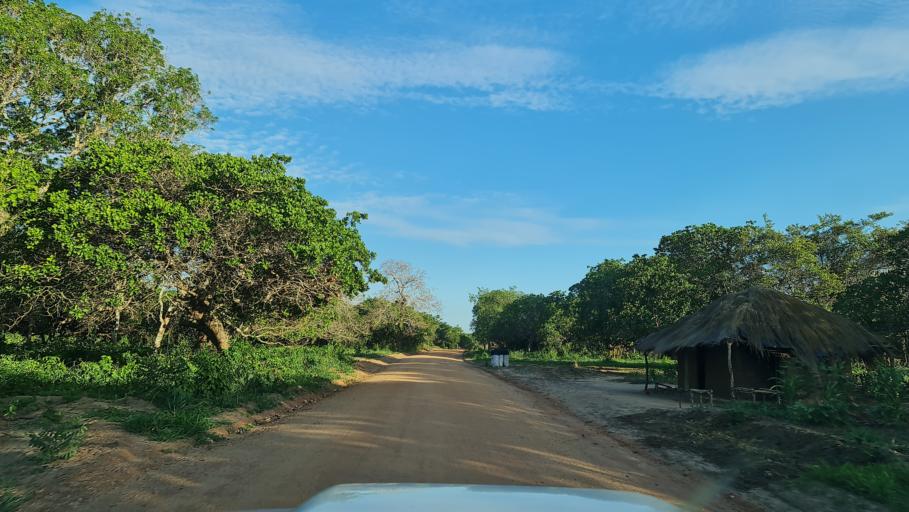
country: MZ
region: Nampula
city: Nacala
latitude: -14.6735
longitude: 40.2887
